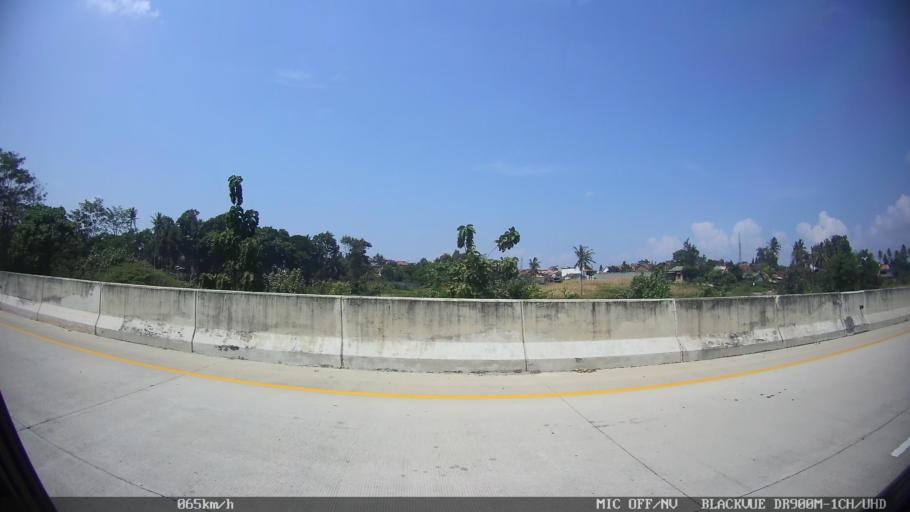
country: ID
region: Lampung
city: Kedaton
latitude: -5.3340
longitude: 105.2976
